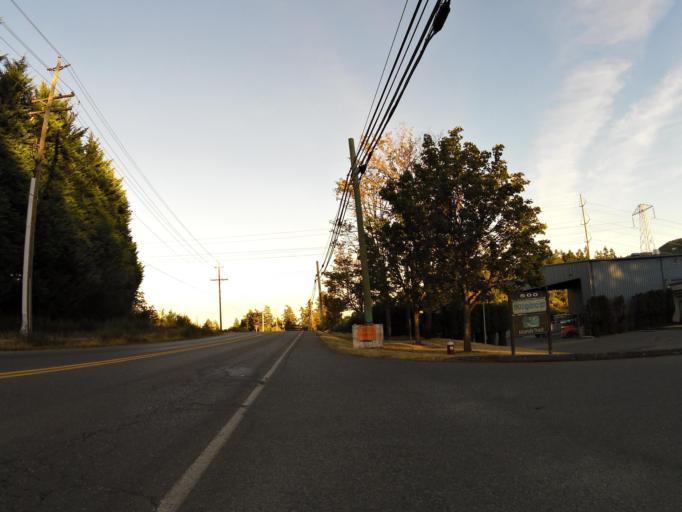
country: CA
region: British Columbia
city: North Cowichan
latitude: 48.8631
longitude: -123.5189
